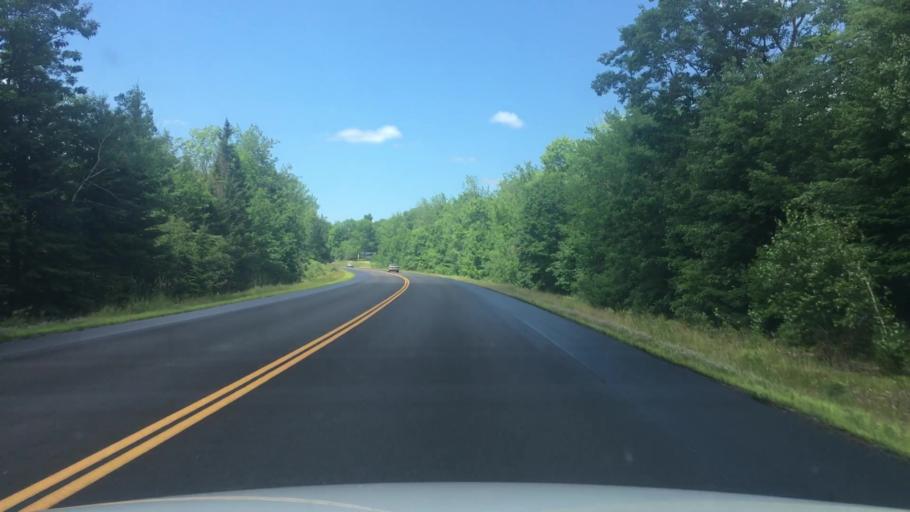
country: US
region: Maine
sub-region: Waldo County
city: Searsmont
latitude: 44.4106
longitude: -69.1807
